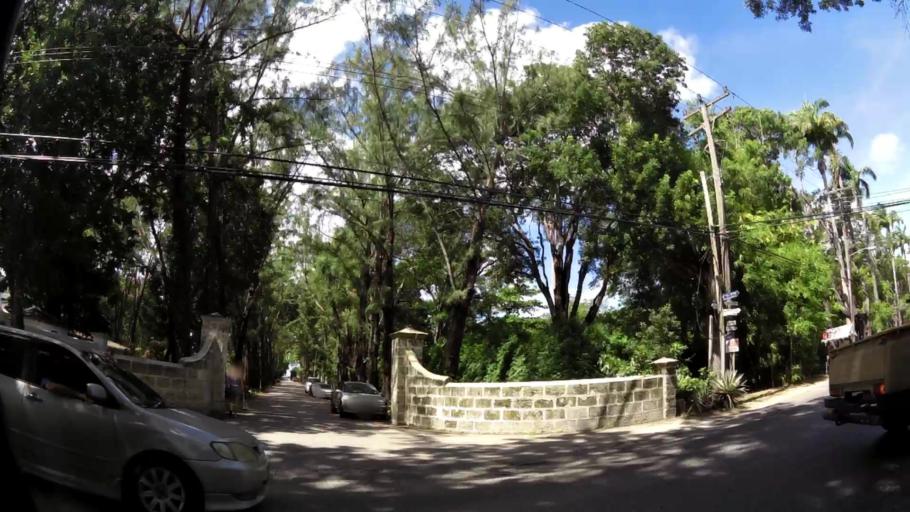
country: BB
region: Saint James
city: Holetown
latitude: 13.1950
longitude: -59.6386
